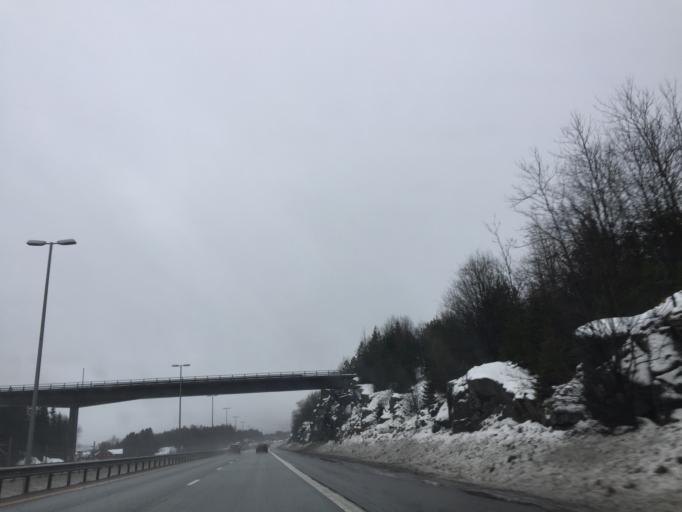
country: NO
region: Akershus
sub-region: Vestby
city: Vestby
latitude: 59.5844
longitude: 10.7335
